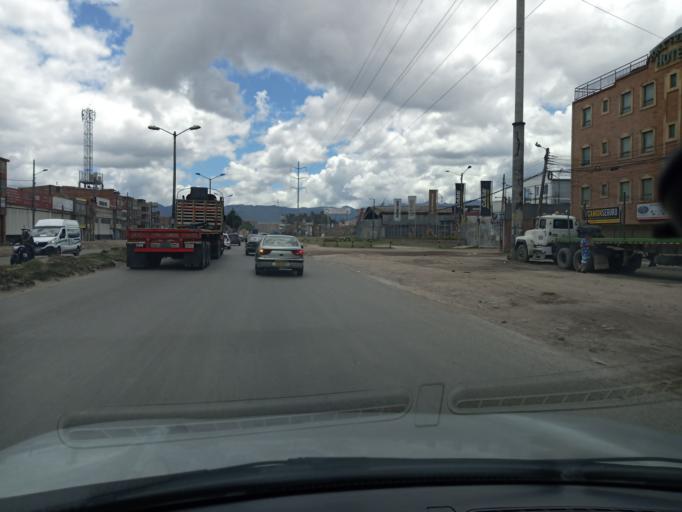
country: CO
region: Cundinamarca
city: Funza
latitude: 4.6664
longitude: -74.1476
